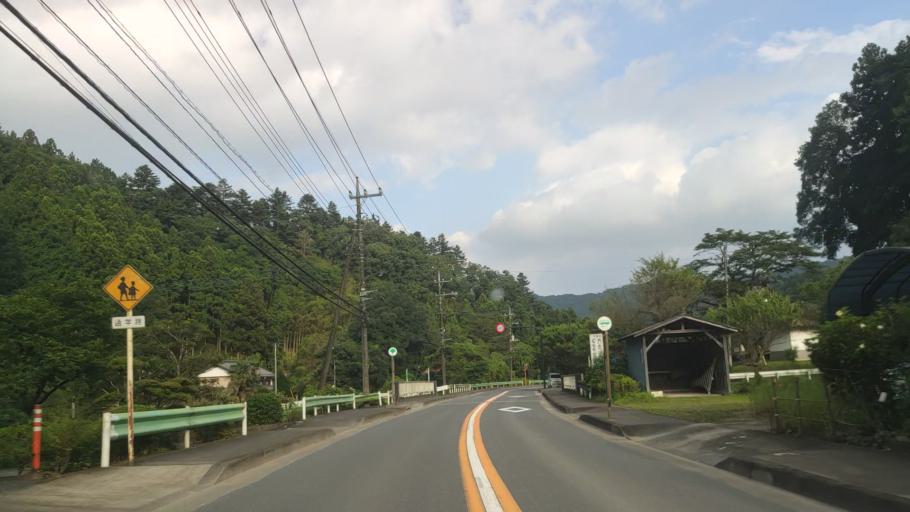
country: JP
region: Tokyo
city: Ome
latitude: 35.8276
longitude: 139.2428
